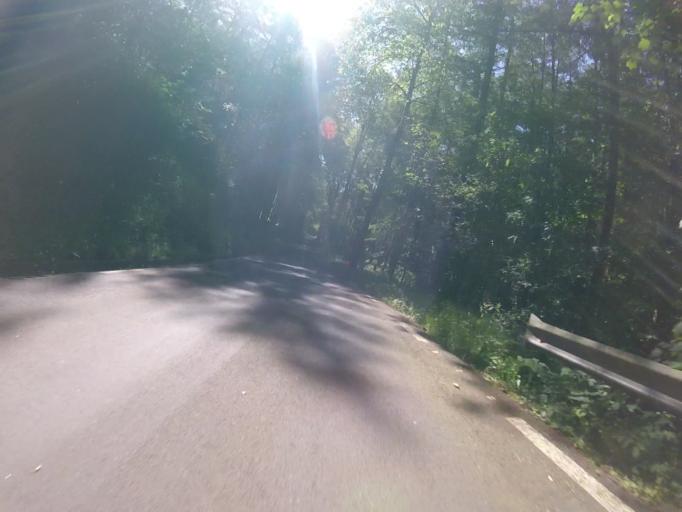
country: ES
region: Basque Country
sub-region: Provincia de Guipuzcoa
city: Albiztur
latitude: 43.1227
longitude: -2.1660
